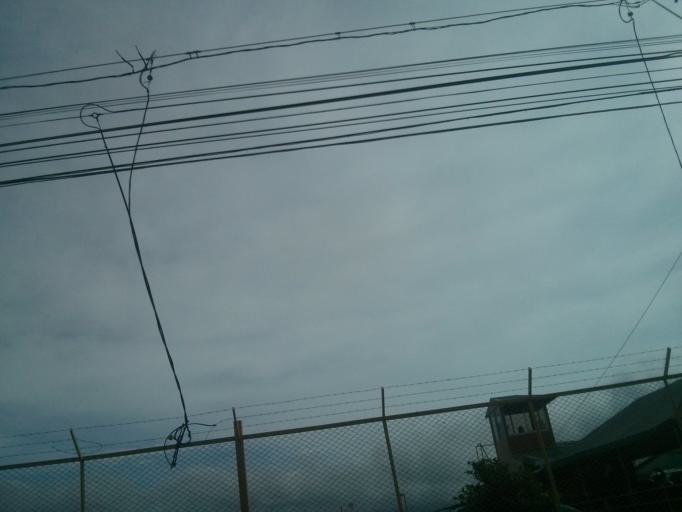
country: CR
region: San Jose
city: Calle Blancos
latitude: 9.9451
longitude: -84.0691
